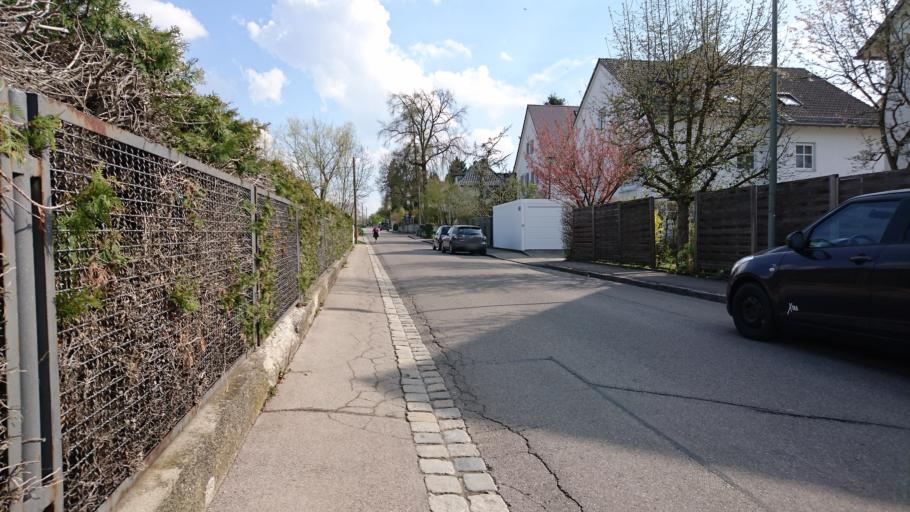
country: DE
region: Bavaria
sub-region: Swabia
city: Stadtbergen
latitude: 48.3770
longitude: 10.8331
